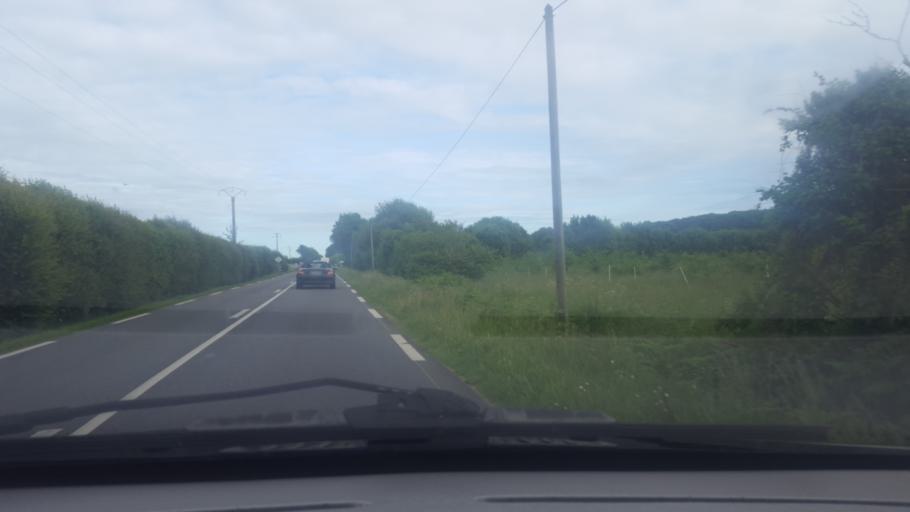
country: FR
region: Pays de la Loire
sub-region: Departement de la Loire-Atlantique
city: Machecoul
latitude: 47.0100
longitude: -1.8501
